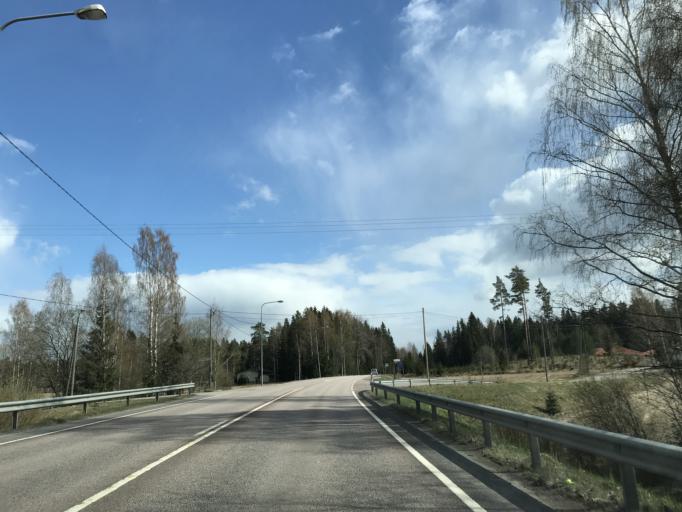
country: FI
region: Uusimaa
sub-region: Helsinki
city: Hyvinge
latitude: 60.5358
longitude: 24.9133
